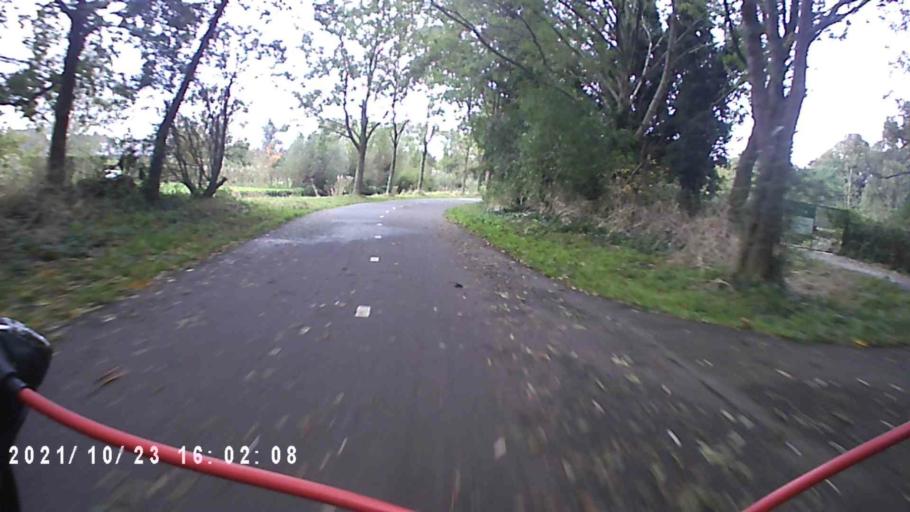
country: NL
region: North Holland
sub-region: Gemeente Langedijk
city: Broek op Langedijk
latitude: 52.6499
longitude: 4.7851
